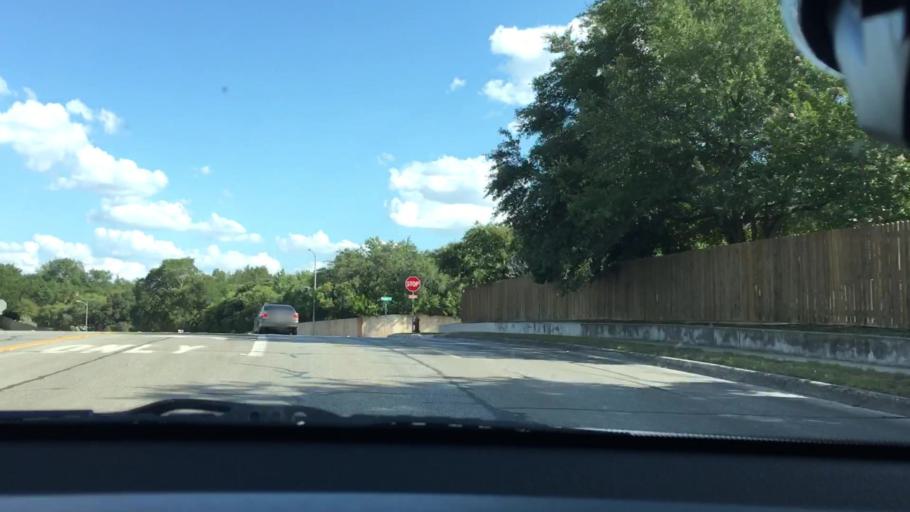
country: US
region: Texas
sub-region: Bexar County
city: Selma
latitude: 29.5615
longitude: -98.3125
